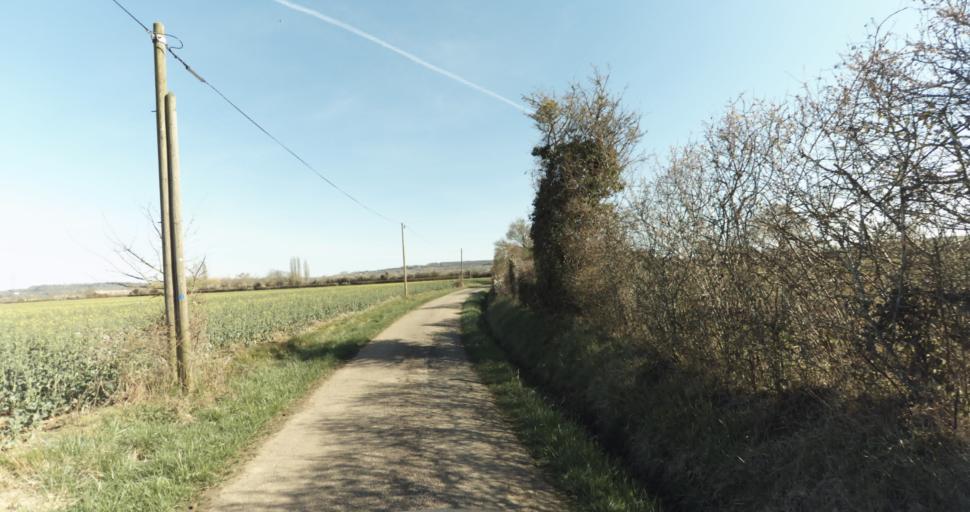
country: FR
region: Lower Normandy
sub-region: Departement du Calvados
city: Saint-Pierre-sur-Dives
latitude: 49.0330
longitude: 0.0095
